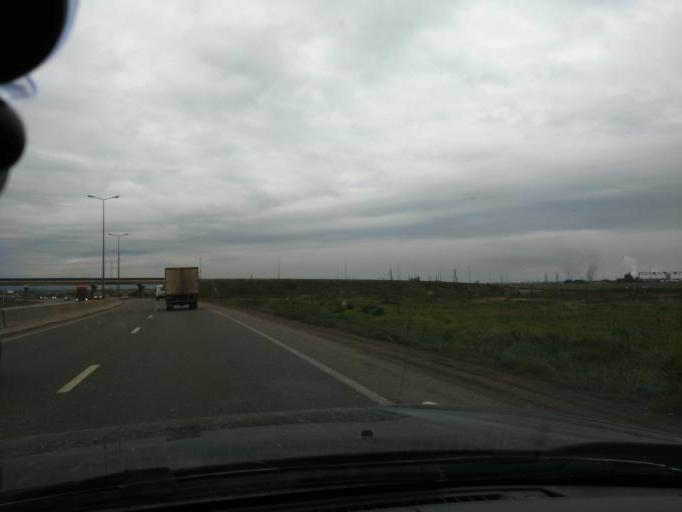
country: RU
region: Perm
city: Kondratovo
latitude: 57.9301
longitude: 56.1691
